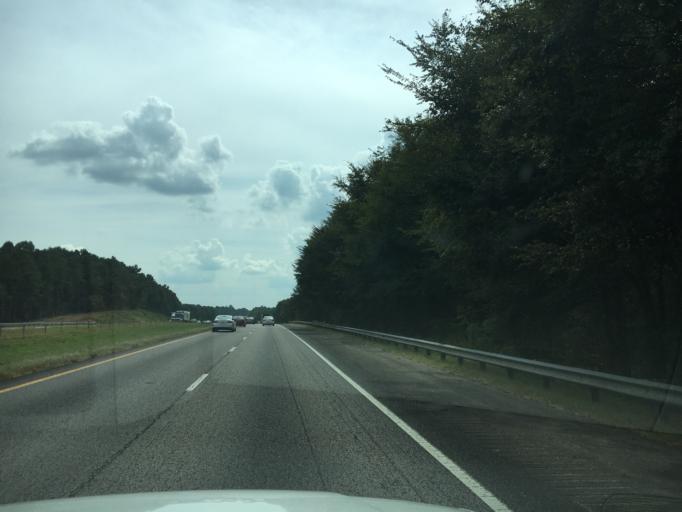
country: US
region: Georgia
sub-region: Jackson County
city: Jefferson
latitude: 34.1747
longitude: -83.6119
